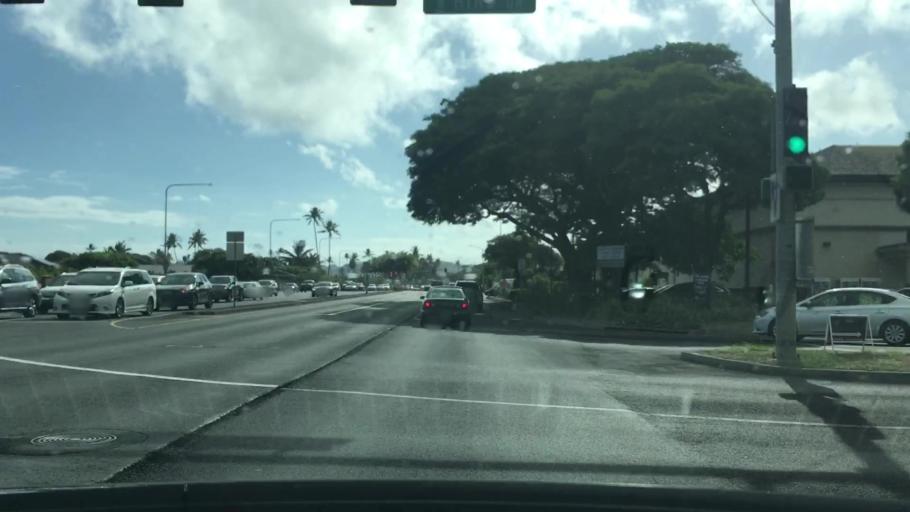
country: US
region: Hawaii
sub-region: Honolulu County
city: Waimanalo
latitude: 21.2779
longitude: -157.7551
